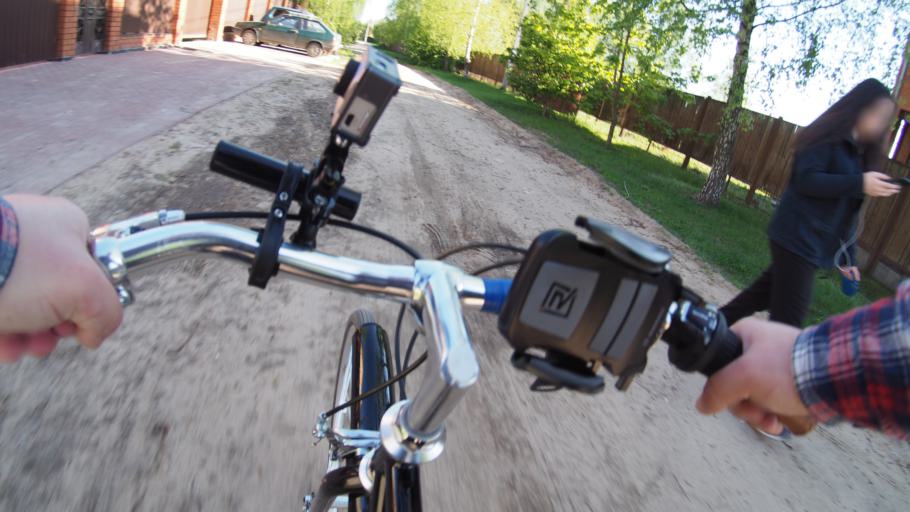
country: RU
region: Moskovskaya
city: Ramenskoye
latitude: 55.5476
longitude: 38.1935
